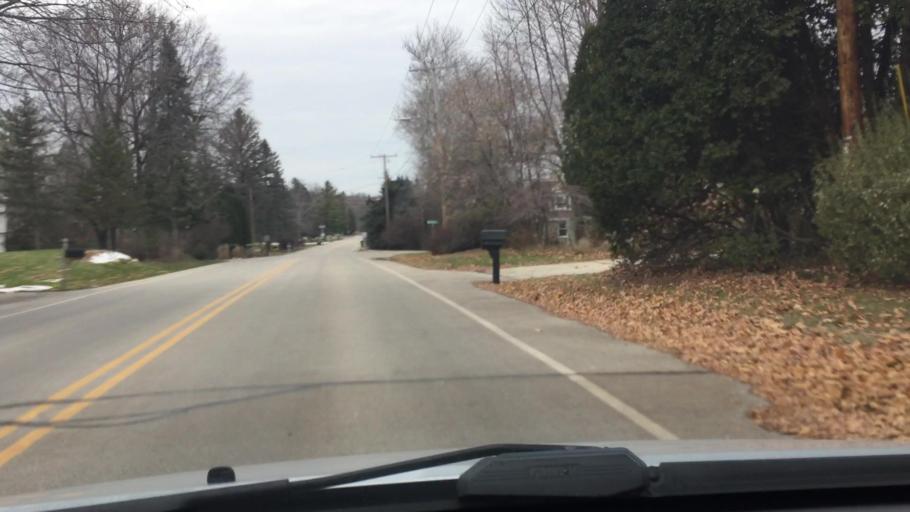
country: US
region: Wisconsin
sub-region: Ozaukee County
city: Thiensville
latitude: 43.2409
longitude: -87.9814
